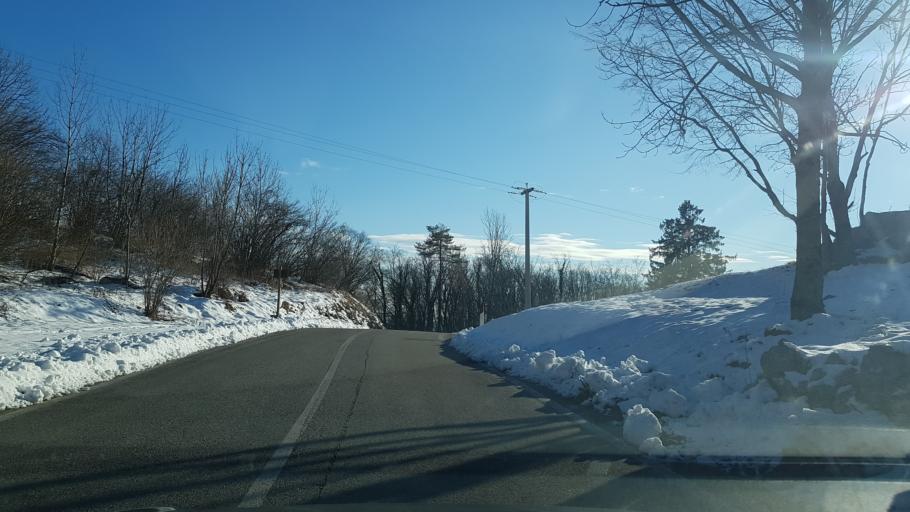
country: IT
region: Friuli Venezia Giulia
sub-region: Provincia di Udine
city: Forgaria nel Friuli
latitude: 46.2409
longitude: 12.9896
